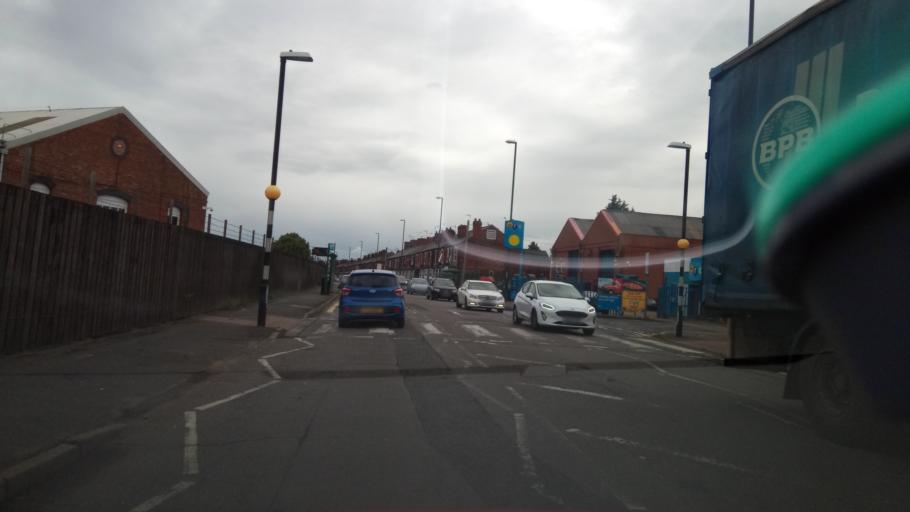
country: GB
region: England
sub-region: Derby
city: Derby
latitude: 52.9036
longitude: -1.4612
